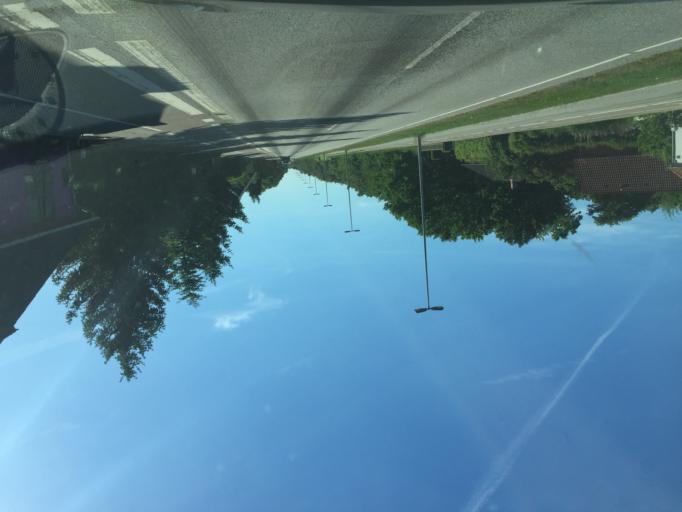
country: DK
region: Zealand
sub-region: Koge Kommune
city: Koge
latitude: 55.4106
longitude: 12.1341
